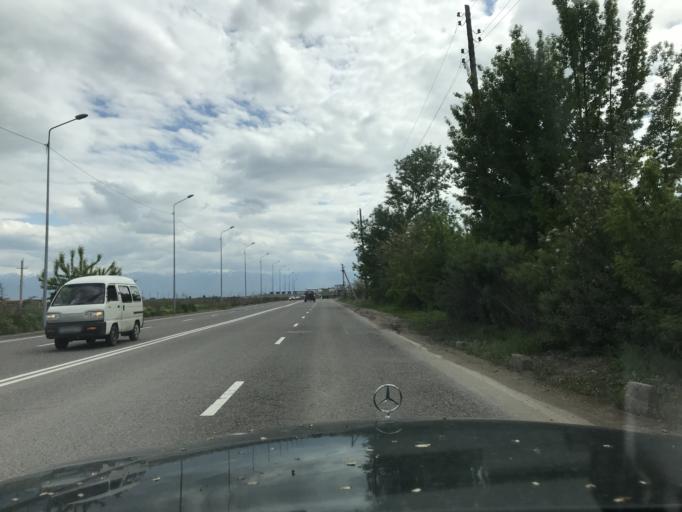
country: KZ
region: Almaty Oblysy
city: Burunday
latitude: 43.3518
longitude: 76.8345
